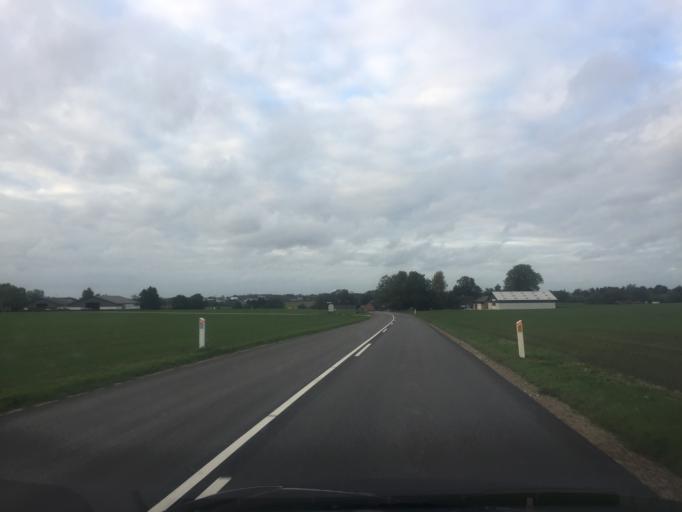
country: DK
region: Zealand
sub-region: Solrod Kommune
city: Havdrup
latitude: 55.5625
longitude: 12.1142
